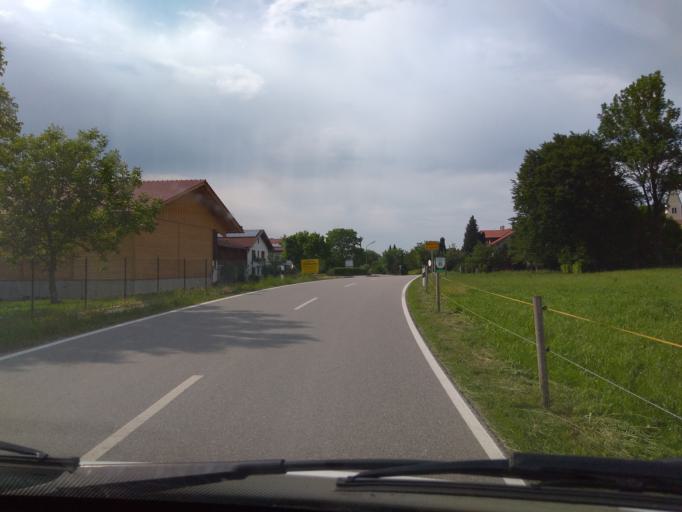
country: DE
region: Bavaria
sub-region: Upper Bavaria
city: Nussdorf am Inn
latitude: 47.7381
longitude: 12.1576
